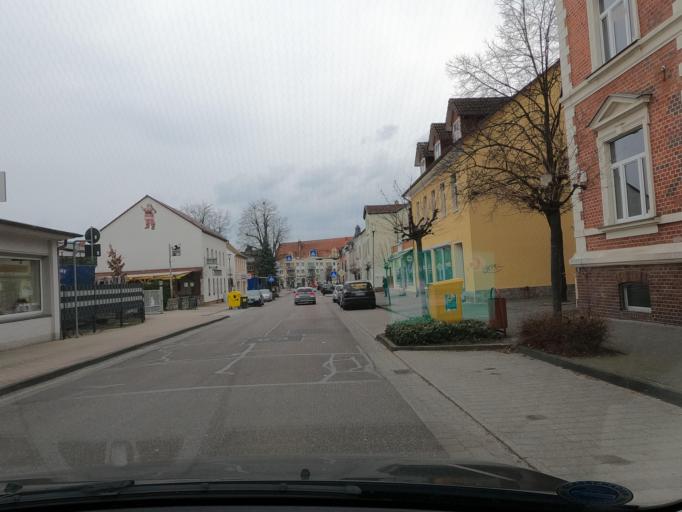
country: DE
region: Saxony
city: Schkeuditz
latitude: 51.3980
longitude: 12.2218
